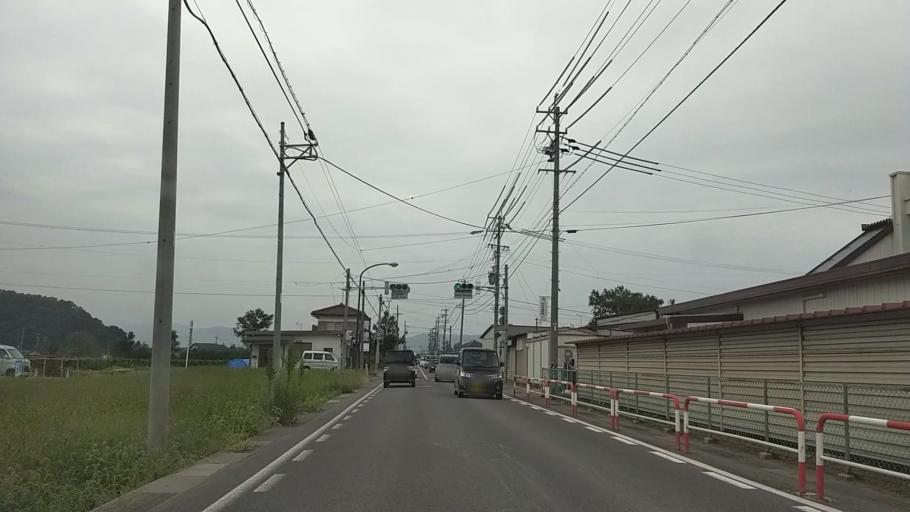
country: JP
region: Nagano
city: Nagano-shi
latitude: 36.5926
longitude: 138.2068
